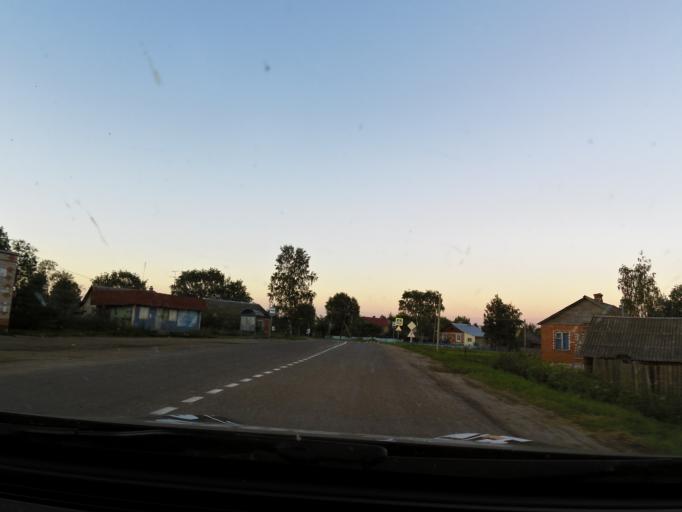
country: RU
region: Jaroslavl
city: Lyubim
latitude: 58.3220
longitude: 41.0064
